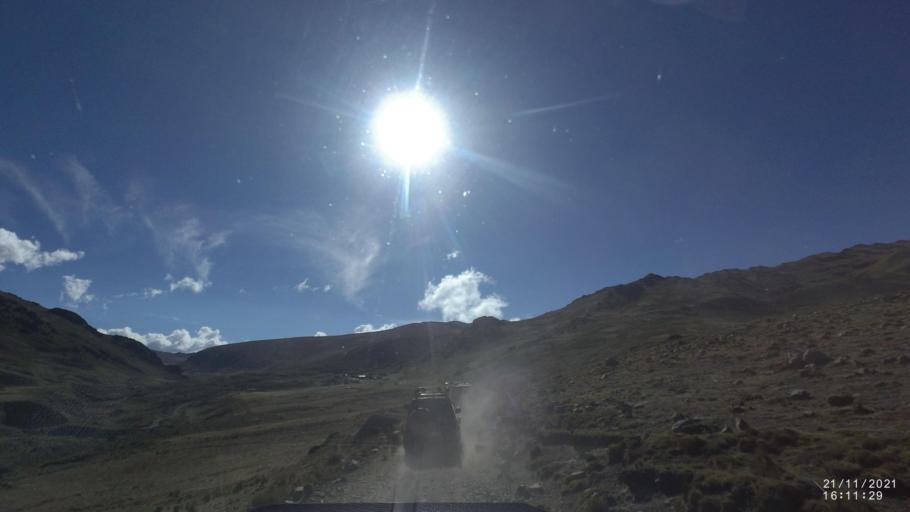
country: BO
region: Cochabamba
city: Cochabamba
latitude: -16.9956
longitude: -66.2714
